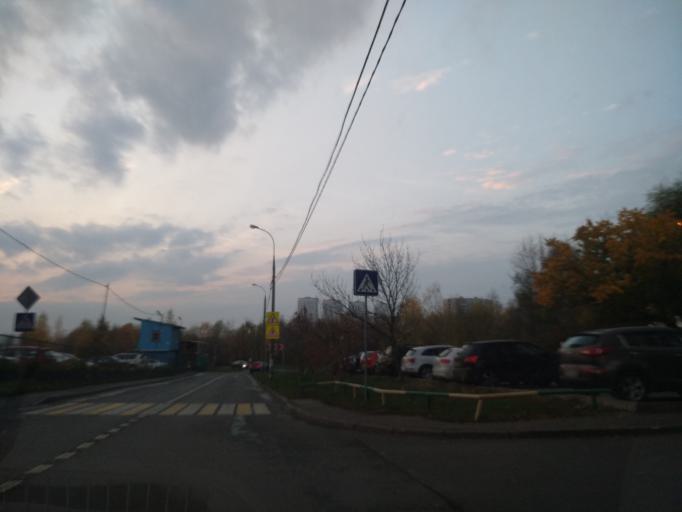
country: RU
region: Moscow
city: Leonovo
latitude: 55.8652
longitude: 37.6503
